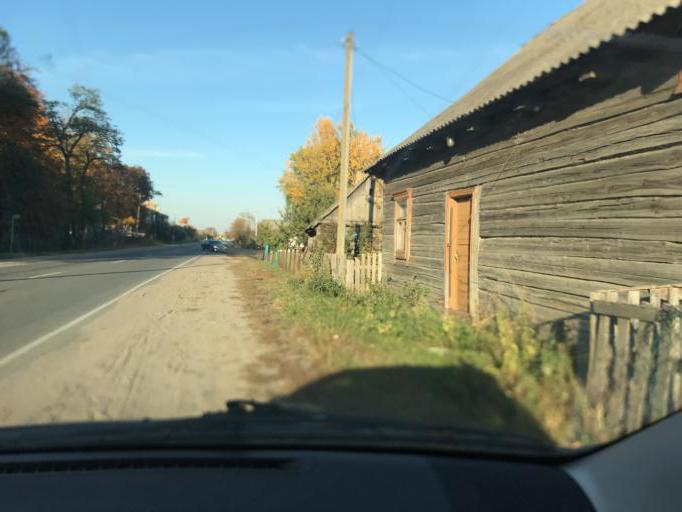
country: BY
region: Brest
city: Stolin
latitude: 51.8528
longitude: 26.7920
